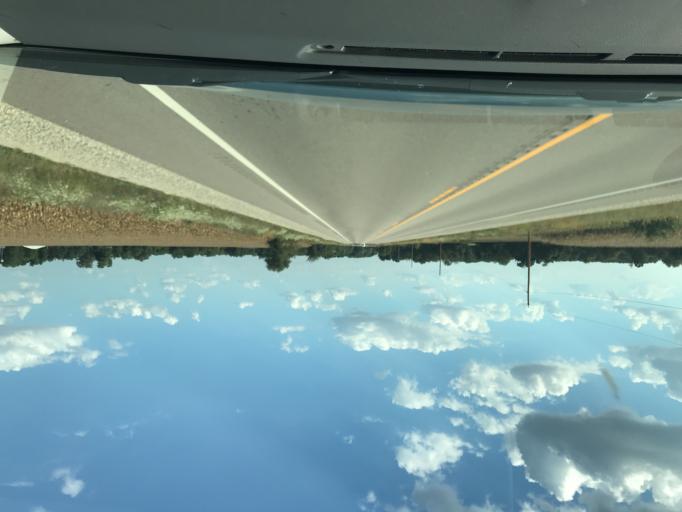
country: US
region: Wisconsin
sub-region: Green County
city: Brodhead
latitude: 42.5792
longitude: -89.3774
